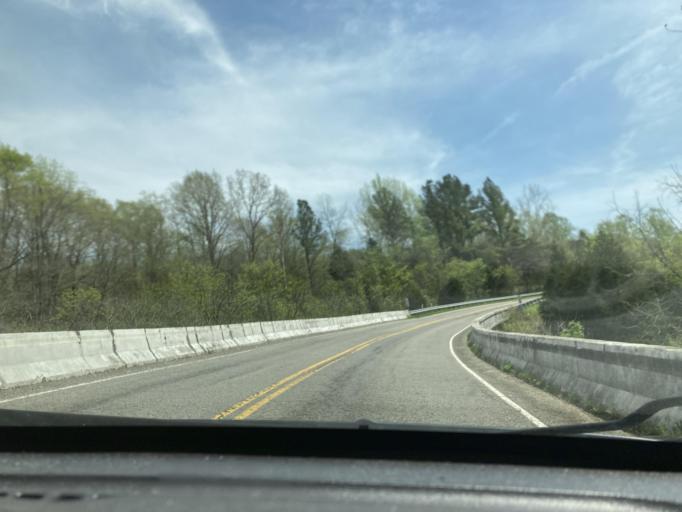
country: US
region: Tennessee
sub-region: Dickson County
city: Charlotte
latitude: 36.2826
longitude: -87.2425
